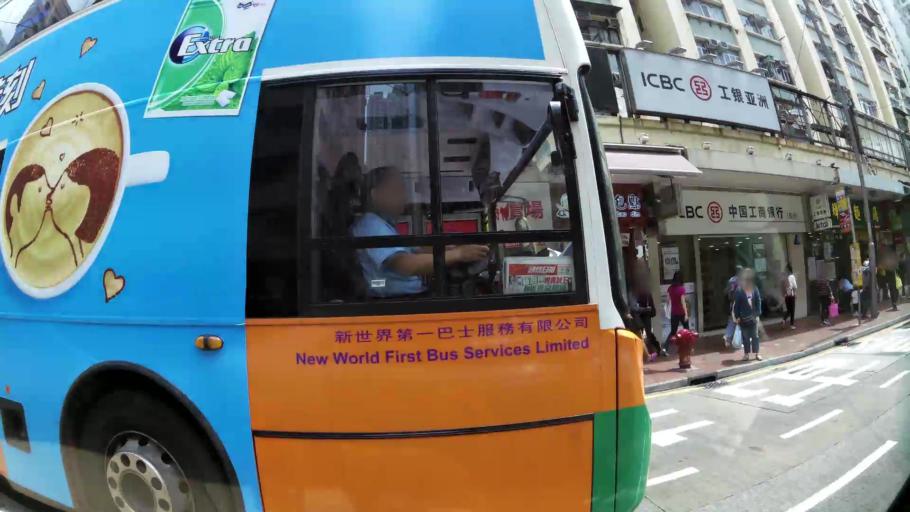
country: HK
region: Wanchai
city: Wan Chai
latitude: 22.2826
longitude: 114.2213
